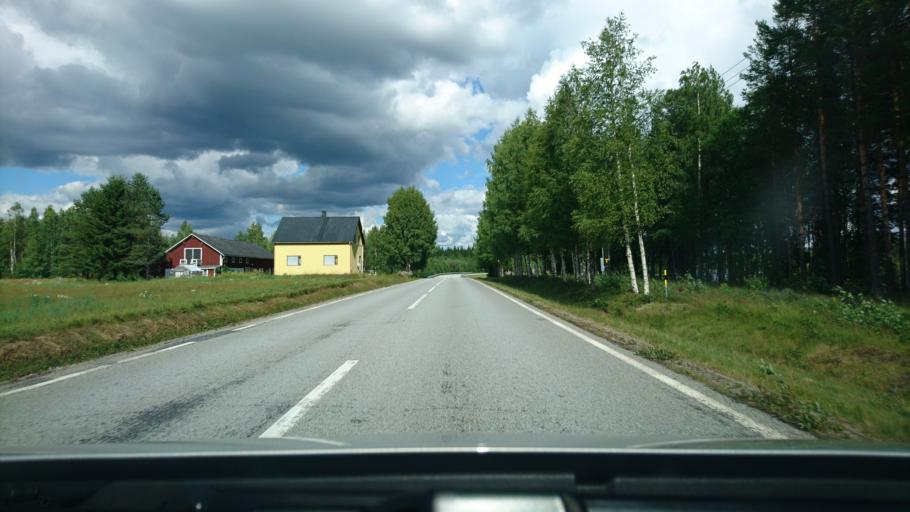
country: SE
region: Vaesterbotten
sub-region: Asele Kommun
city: Asele
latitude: 63.7846
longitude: 17.0421
